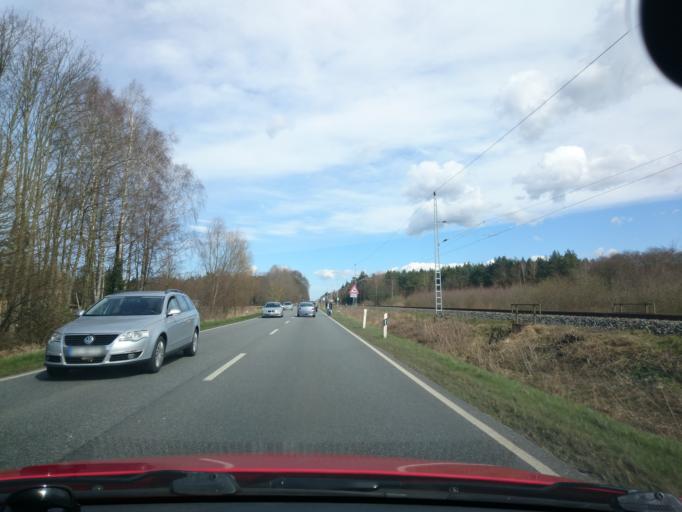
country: DE
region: Mecklenburg-Vorpommern
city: Rovershagen
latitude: 54.1826
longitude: 12.2631
